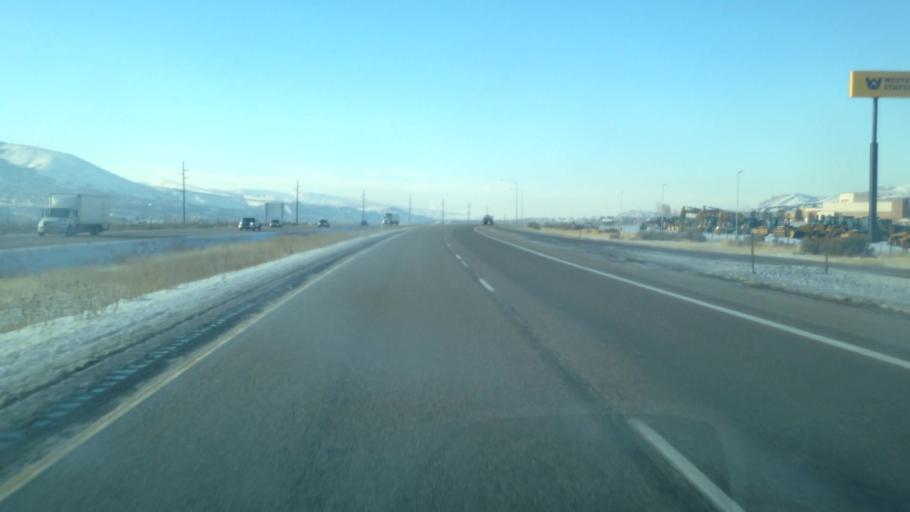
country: US
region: Idaho
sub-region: Bannock County
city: Pocatello
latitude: 42.8022
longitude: -112.3693
